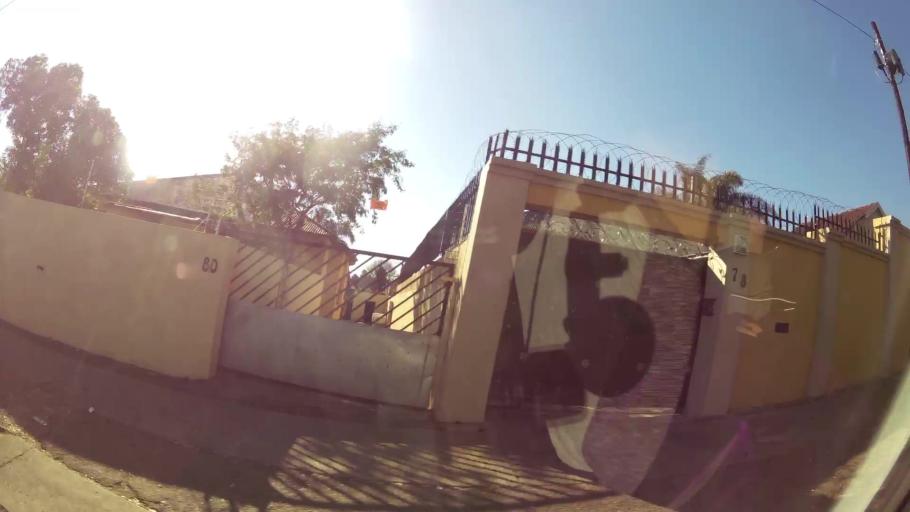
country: ZA
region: Gauteng
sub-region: City of Johannesburg Metropolitan Municipality
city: Johannesburg
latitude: -26.1986
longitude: 28.0963
